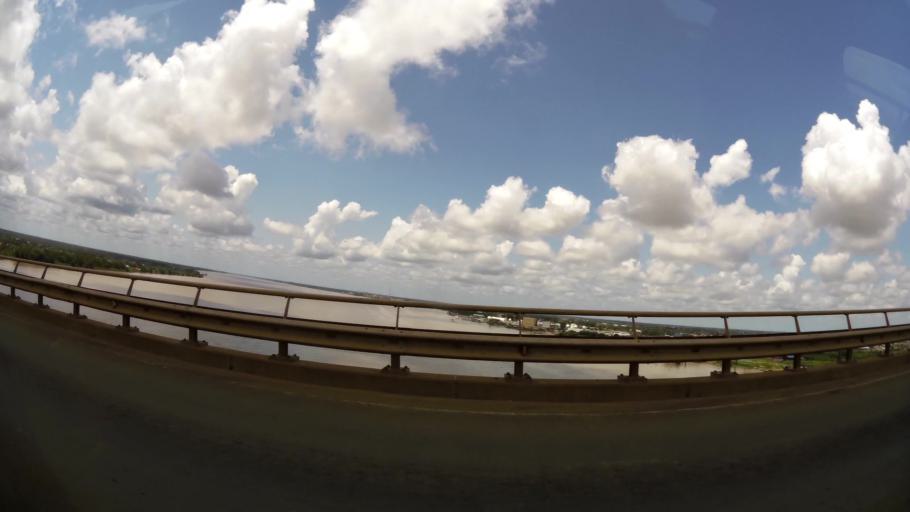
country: SR
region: Paramaribo
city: Paramaribo
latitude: 5.8057
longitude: -55.1630
